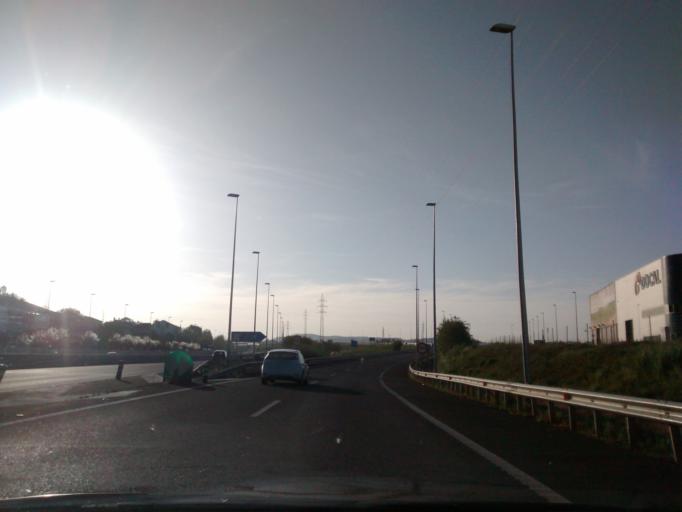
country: ES
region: Cantabria
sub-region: Provincia de Cantabria
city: El Astillero
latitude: 43.3950
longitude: -3.7992
